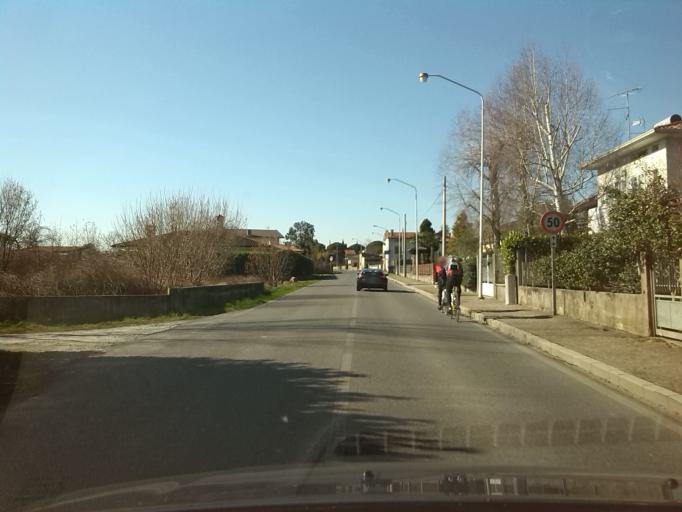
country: IT
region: Friuli Venezia Giulia
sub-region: Provincia di Udine
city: Faedis
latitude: 46.1265
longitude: 13.3683
